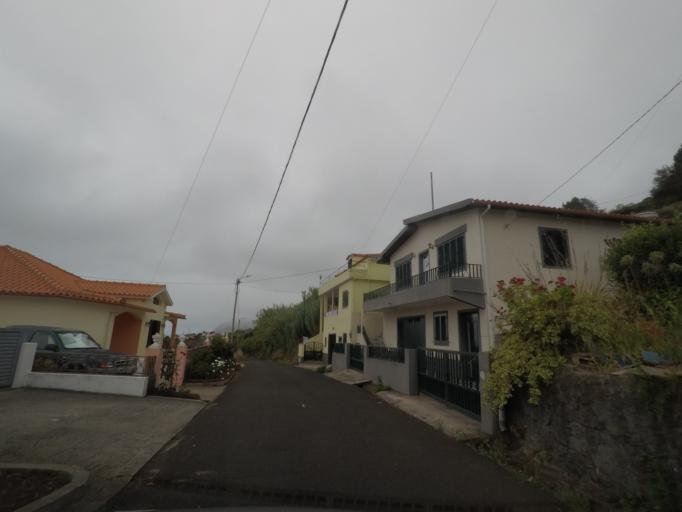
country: PT
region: Madeira
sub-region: Santana
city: Santana
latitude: 32.7679
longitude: -16.8487
